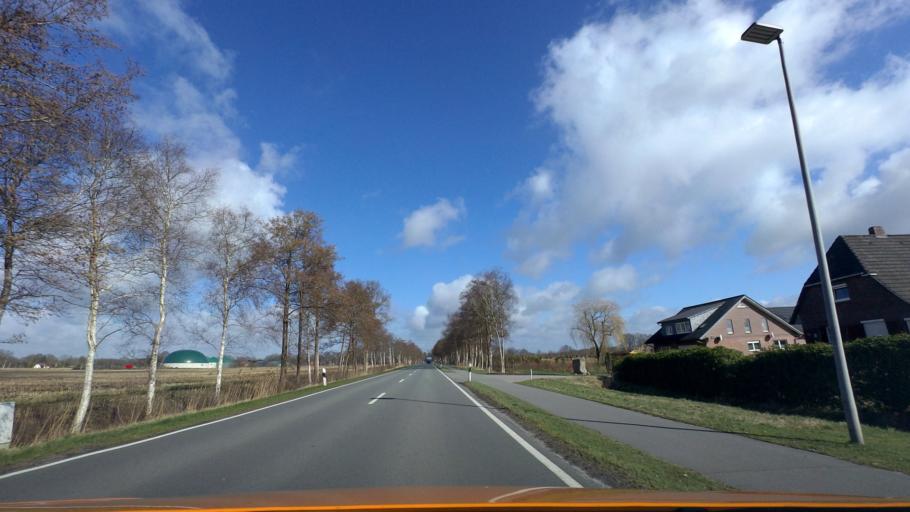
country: DE
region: Lower Saxony
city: Edewecht
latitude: 53.0941
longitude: 7.9456
